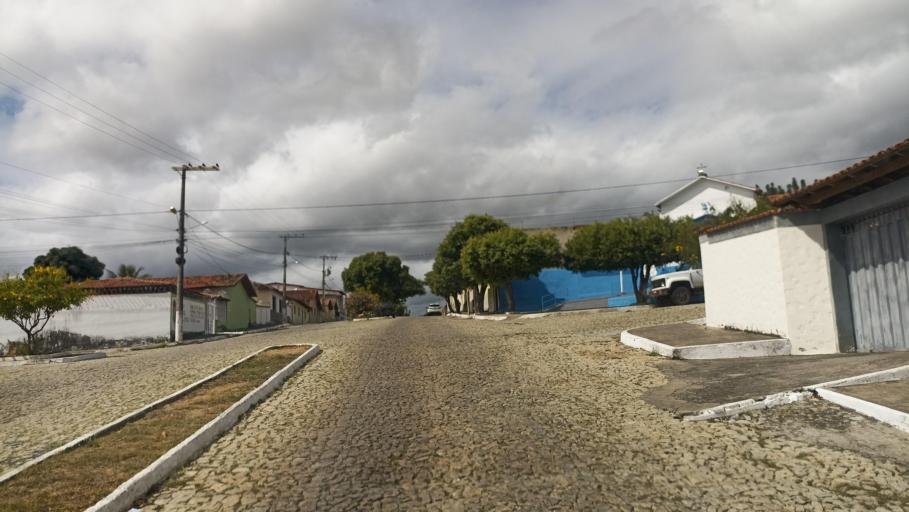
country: BR
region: Minas Gerais
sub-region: Jequitinhonha
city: Jequitinhonha
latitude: -16.4376
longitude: -41.0082
